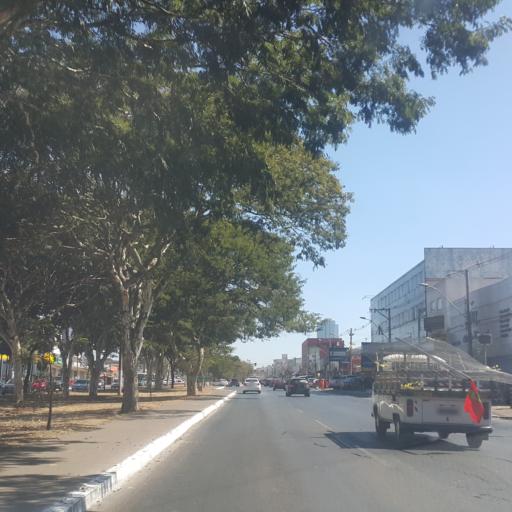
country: BR
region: Federal District
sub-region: Brasilia
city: Brasilia
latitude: -15.8067
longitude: -48.0794
